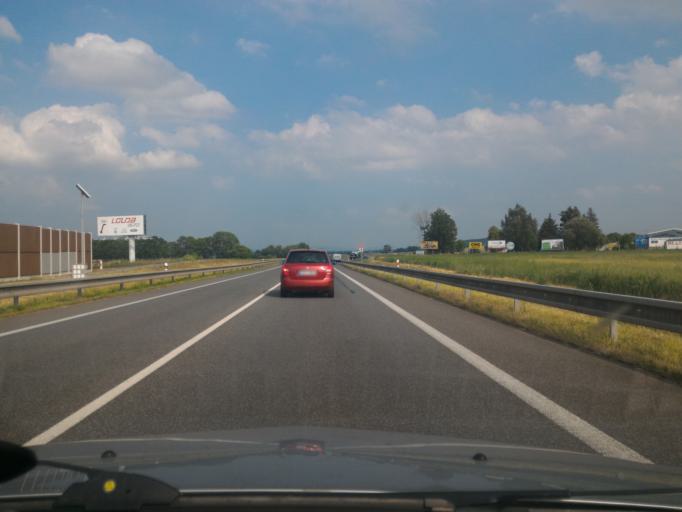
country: CZ
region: Central Bohemia
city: Cervene Pecky
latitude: 50.0040
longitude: 15.2353
